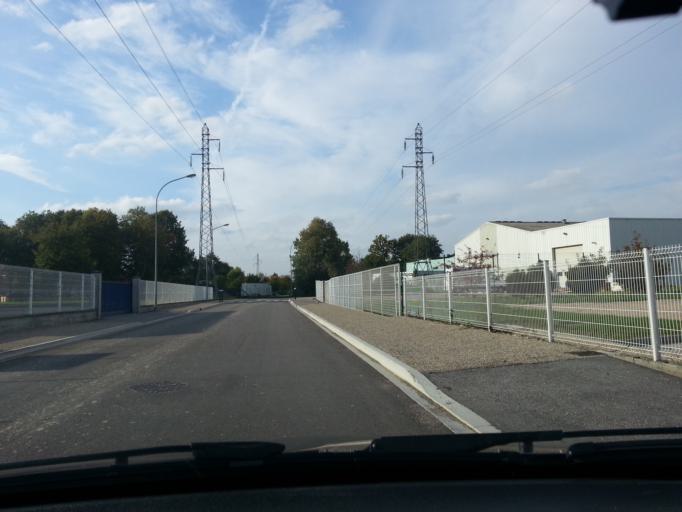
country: FR
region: Bourgogne
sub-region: Departement de Saone-et-Loire
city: Chatenoy-le-Royal
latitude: 46.7973
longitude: 4.7893
